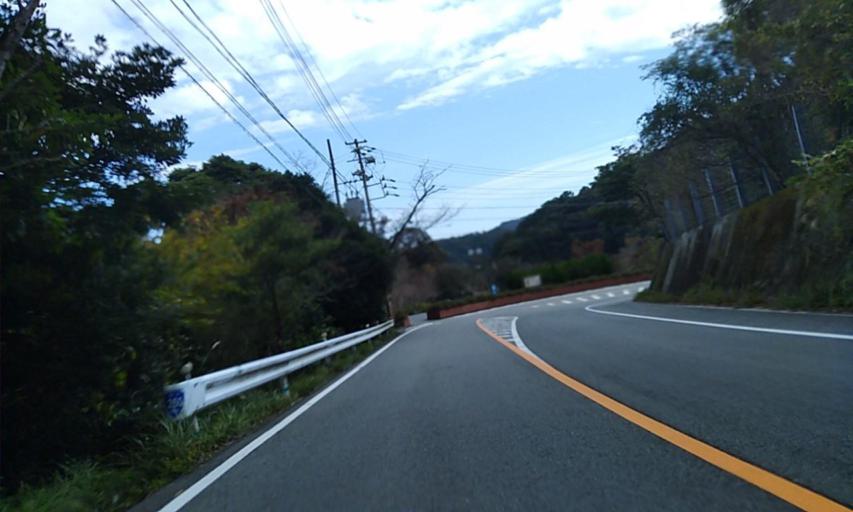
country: JP
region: Mie
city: Ise
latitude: 34.2869
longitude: 136.5369
